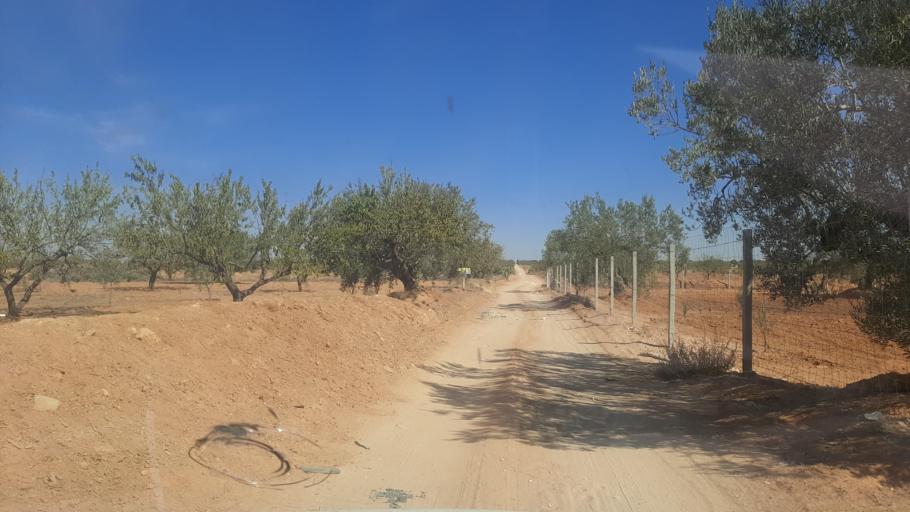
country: TN
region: Safaqis
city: Sfax
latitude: 34.8723
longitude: 10.5628
